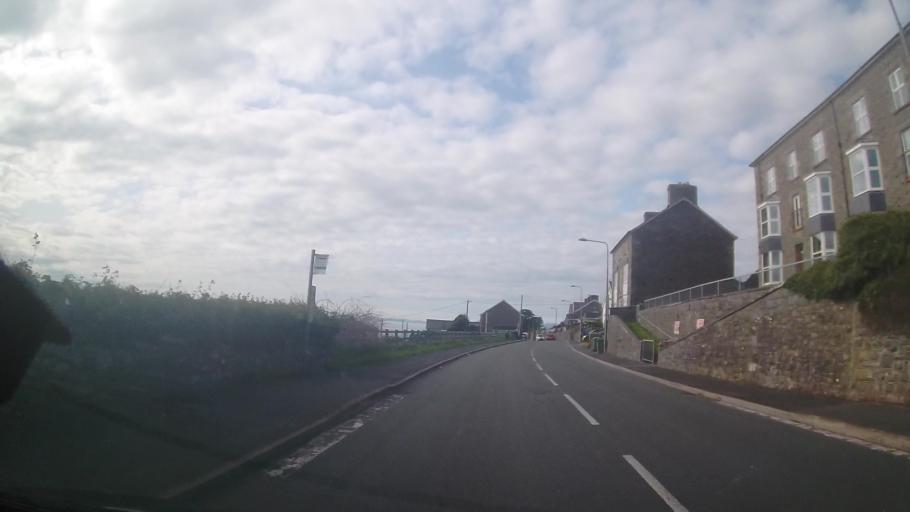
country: GB
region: Wales
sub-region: Gwynedd
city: Barmouth
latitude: 52.7361
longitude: -4.0691
